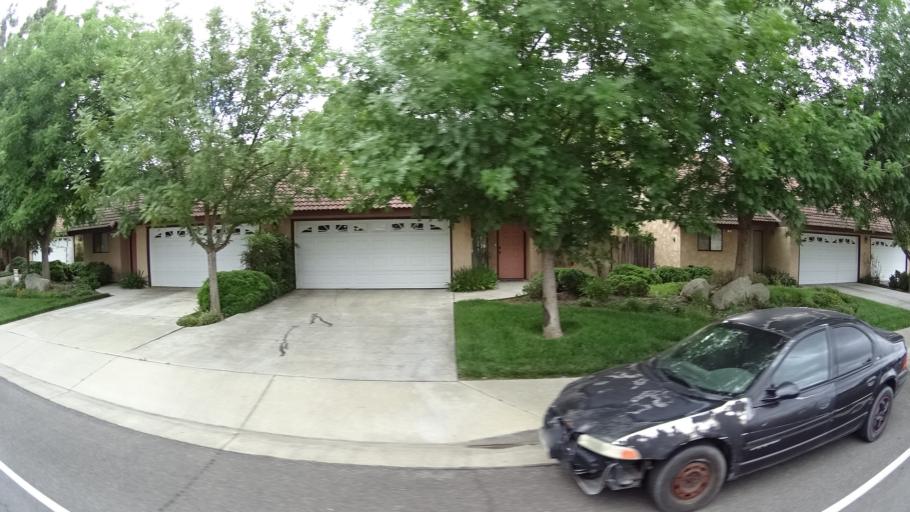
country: US
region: California
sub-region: Kings County
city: Hanford
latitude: 36.3440
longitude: -119.6595
